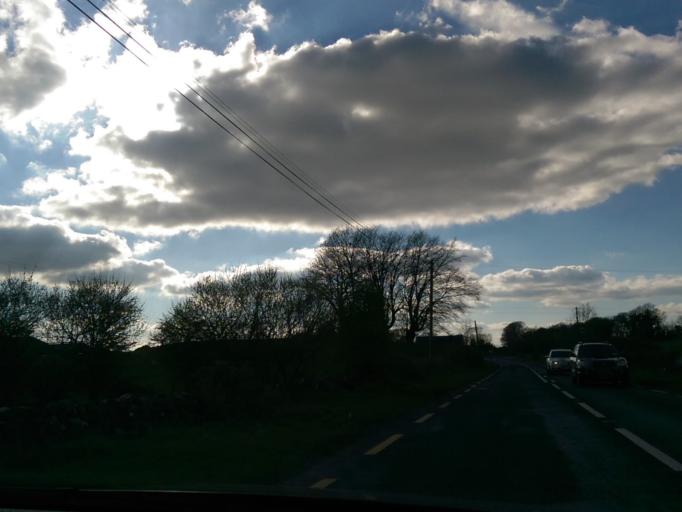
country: IE
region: Connaught
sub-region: County Galway
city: Loughrea
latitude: 53.1990
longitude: -8.4268
